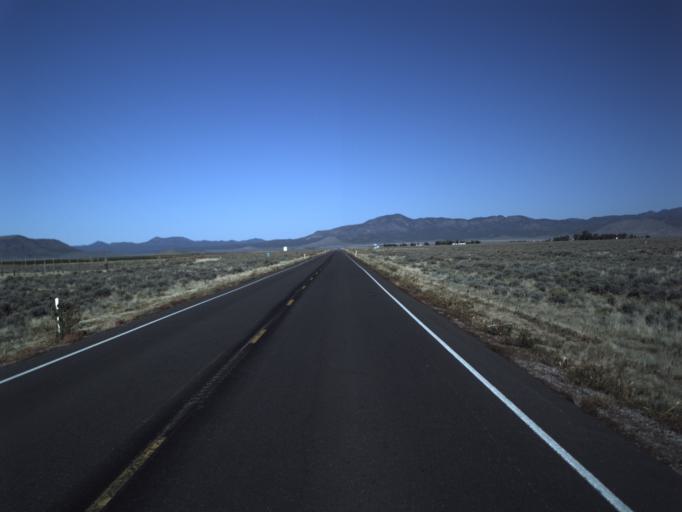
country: US
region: Utah
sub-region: Washington County
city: Enterprise
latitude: 37.7569
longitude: -113.7898
